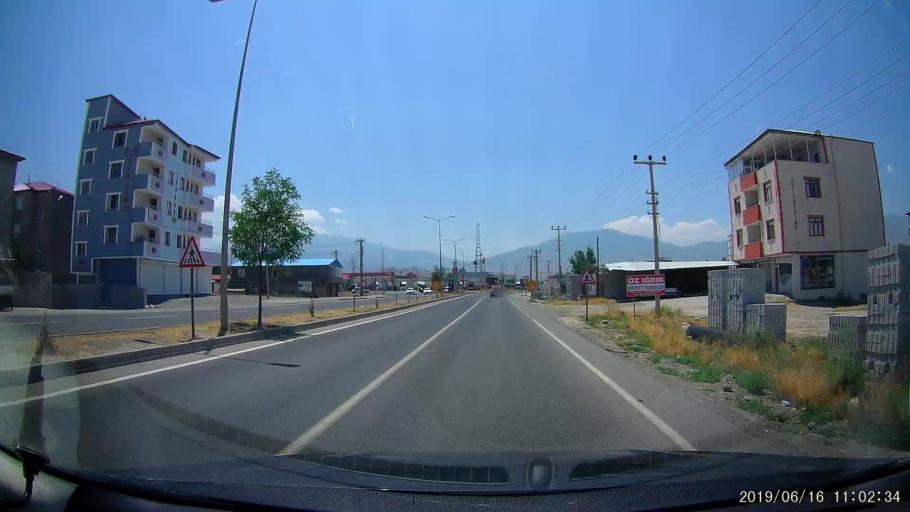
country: TR
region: Igdir
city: Igdir
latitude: 39.9109
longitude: 44.0586
